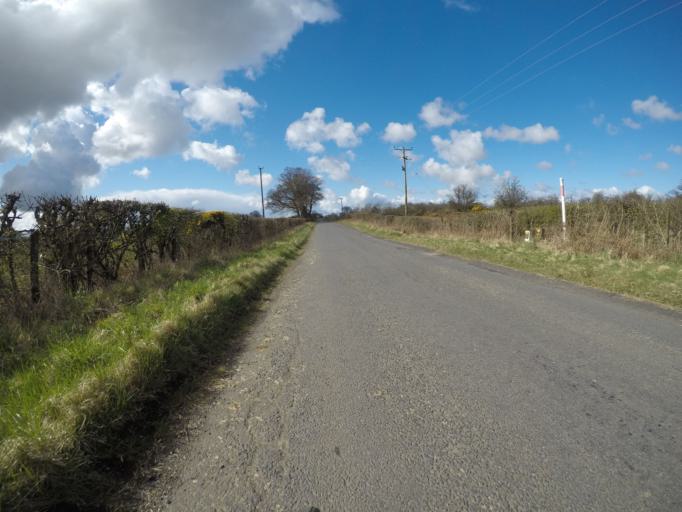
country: GB
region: Scotland
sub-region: North Ayrshire
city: Kilbirnie
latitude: 55.7175
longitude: -4.6795
